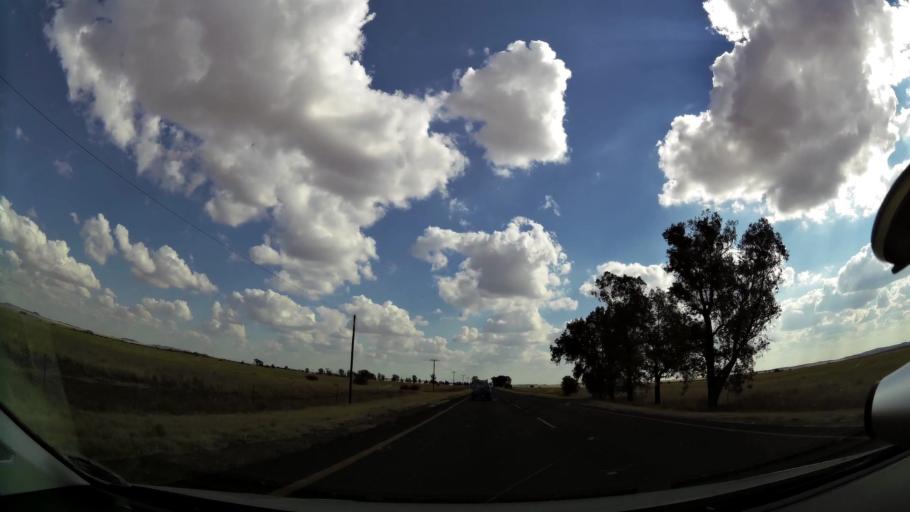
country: ZA
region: Orange Free State
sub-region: Xhariep District Municipality
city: Koffiefontein
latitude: -29.1319
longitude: 25.5350
